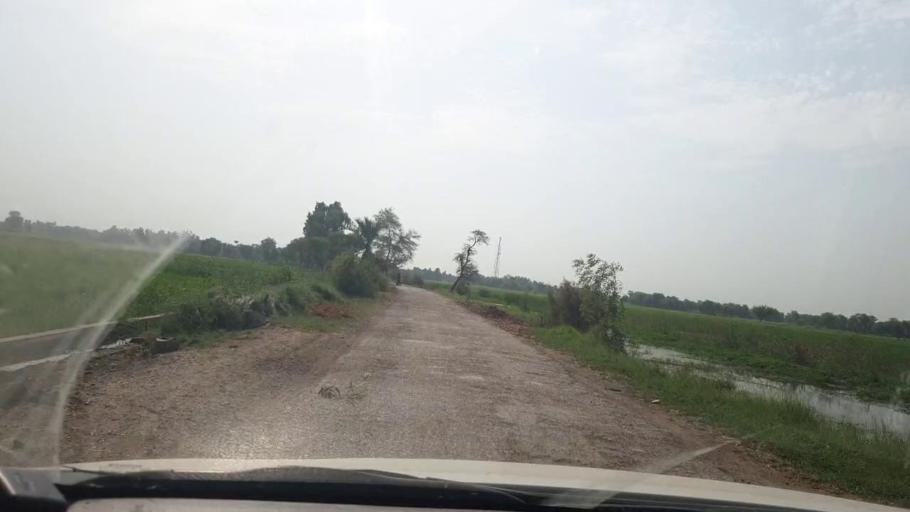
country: PK
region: Sindh
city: Chak
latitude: 27.8312
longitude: 68.7689
